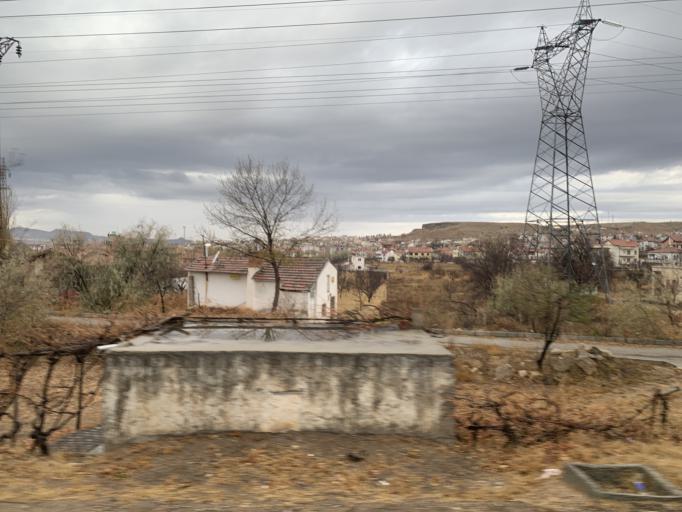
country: TR
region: Nevsehir
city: Avanos
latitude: 38.7178
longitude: 34.8602
